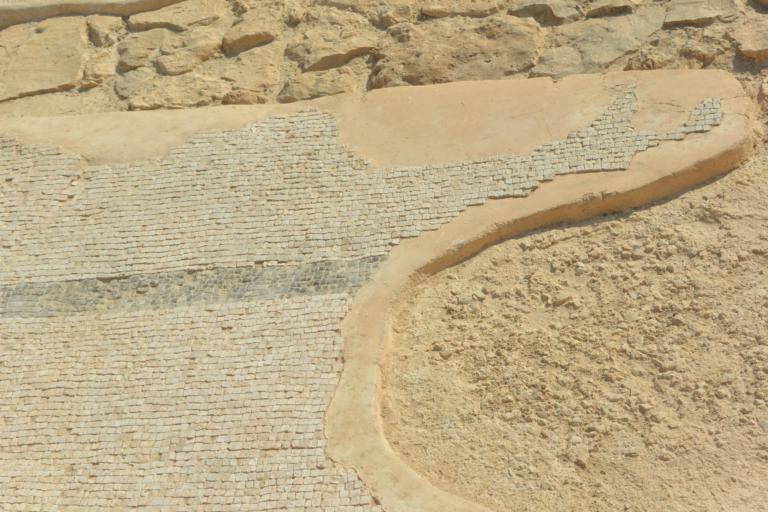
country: IL
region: Southern District
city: `En Boqeq
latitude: 31.3182
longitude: 35.3541
